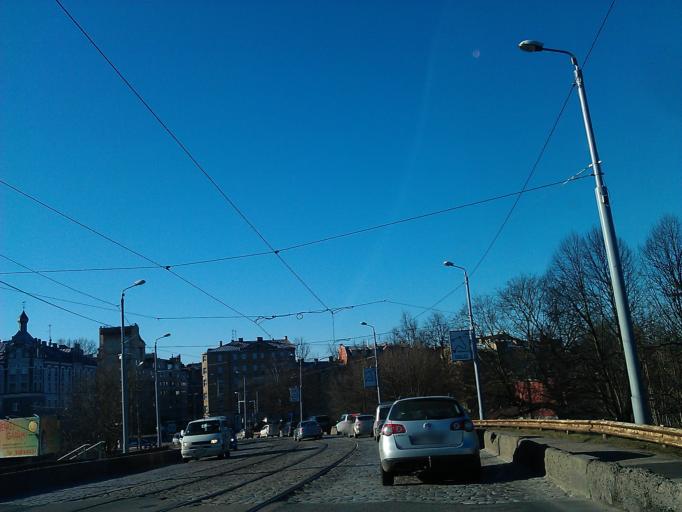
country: LV
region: Riga
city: Riga
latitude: 56.9779
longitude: 24.1455
